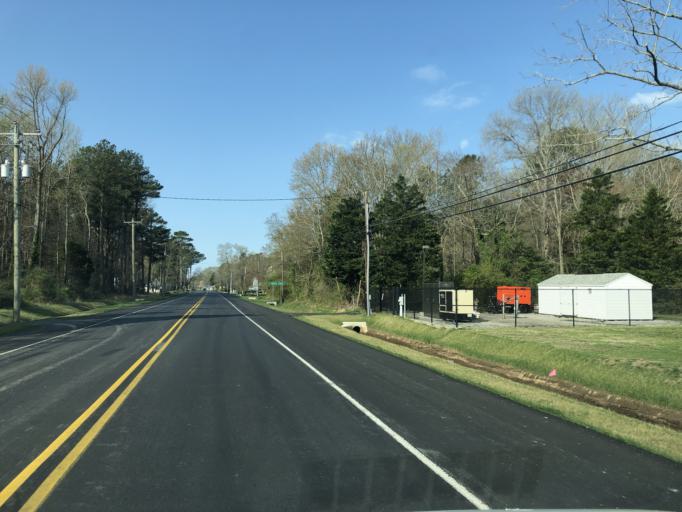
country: US
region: Maryland
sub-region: Dorchester County
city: Algonquin
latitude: 38.5119
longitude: -76.1400
